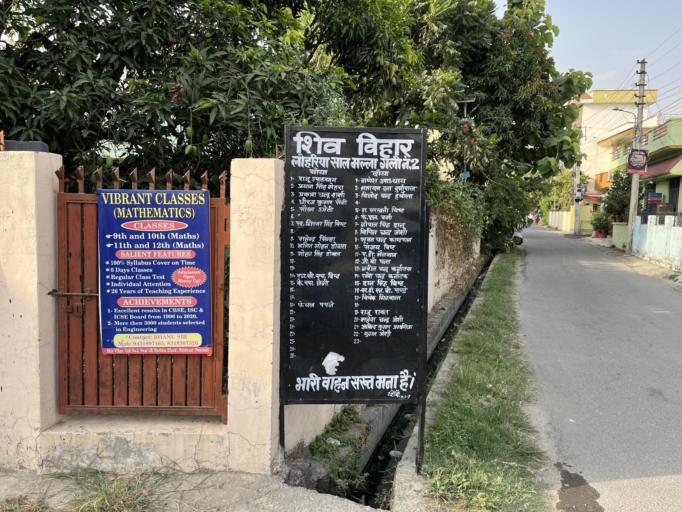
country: IN
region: Uttarakhand
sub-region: Naini Tal
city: Haldwani
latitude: 29.2317
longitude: 79.4885
